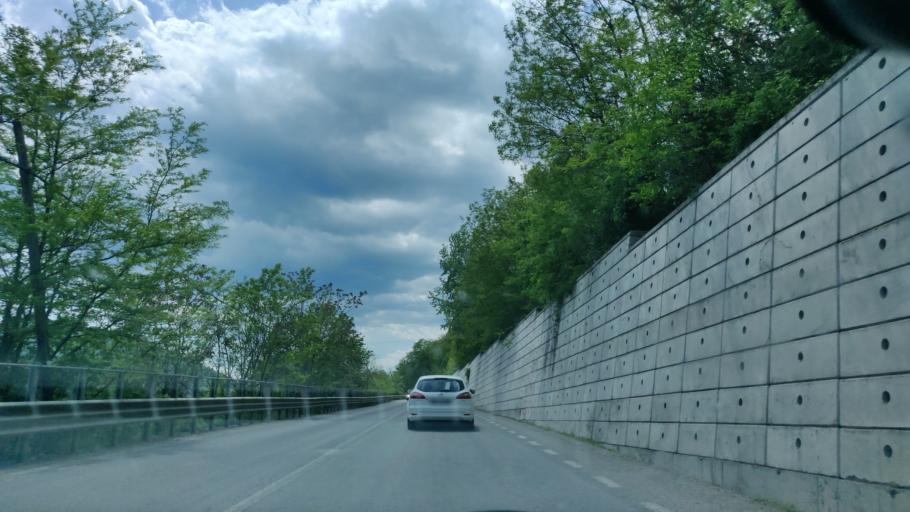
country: RO
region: Vrancea
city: Matacina
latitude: 45.8871
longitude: 26.8124
